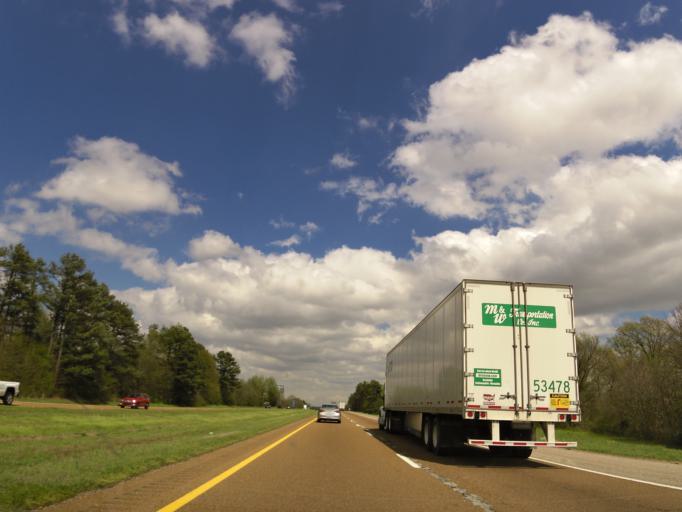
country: US
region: Tennessee
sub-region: Tipton County
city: Mason
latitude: 35.3507
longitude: -89.5142
